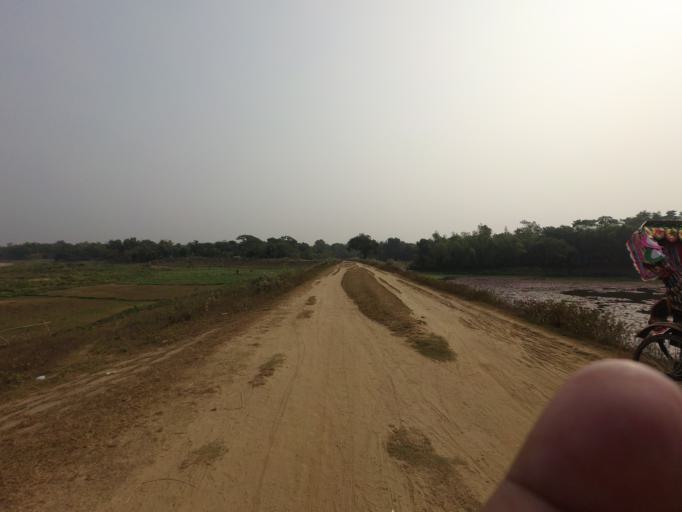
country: BD
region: Dhaka
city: Netrakona
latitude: 25.1079
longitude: 90.6663
